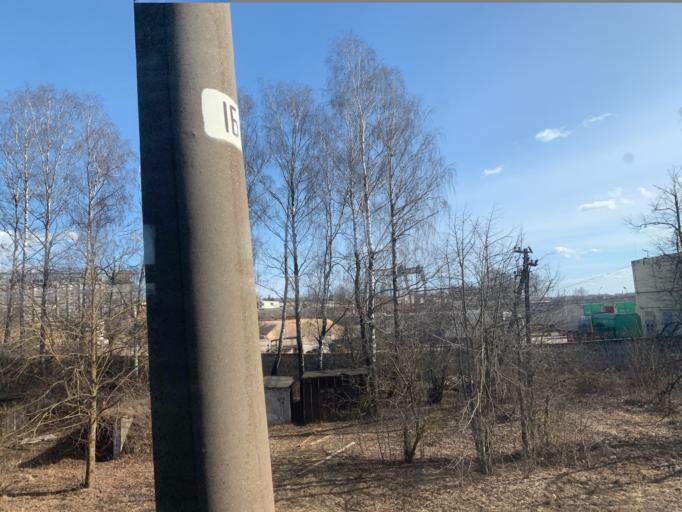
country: BY
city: Fanipol
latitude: 53.7385
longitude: 27.3222
